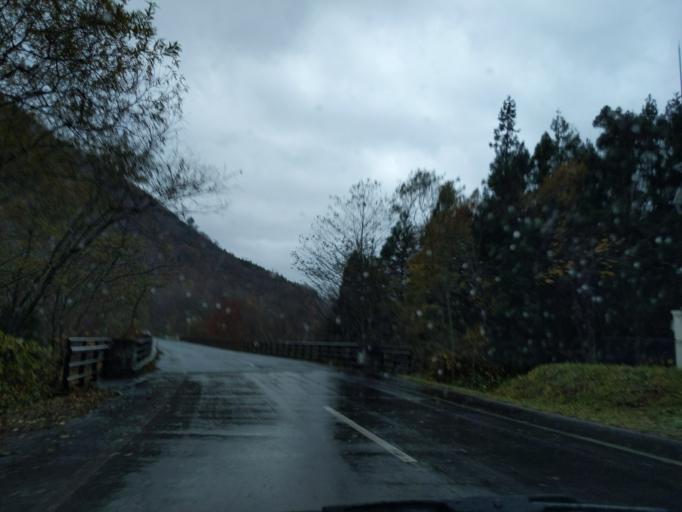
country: JP
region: Iwate
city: Mizusawa
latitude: 39.0537
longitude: 140.8542
